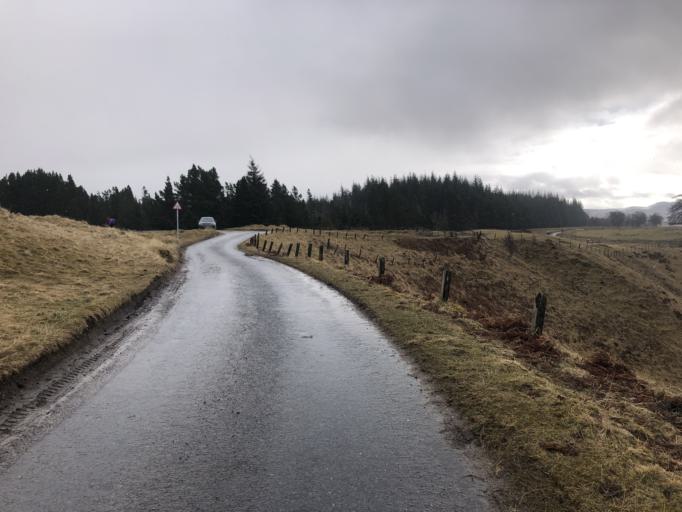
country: GB
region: Scotland
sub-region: Highland
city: Kingussie
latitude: 57.0713
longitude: -4.1427
